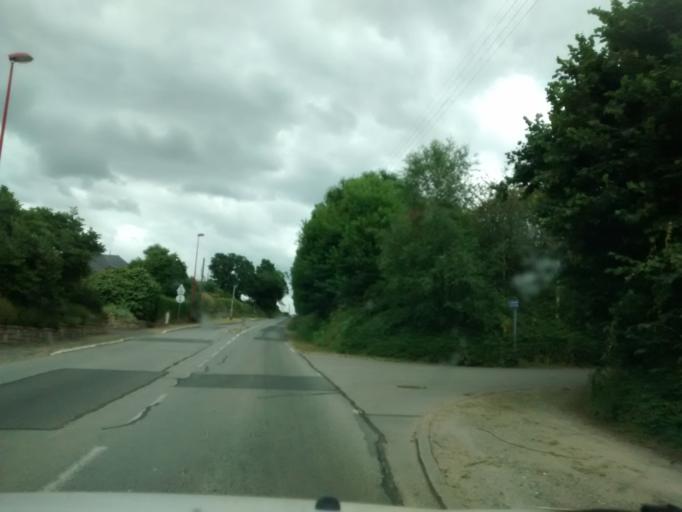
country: FR
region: Brittany
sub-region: Departement du Finistere
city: Ploudaniel
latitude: 48.5596
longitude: -4.2619
